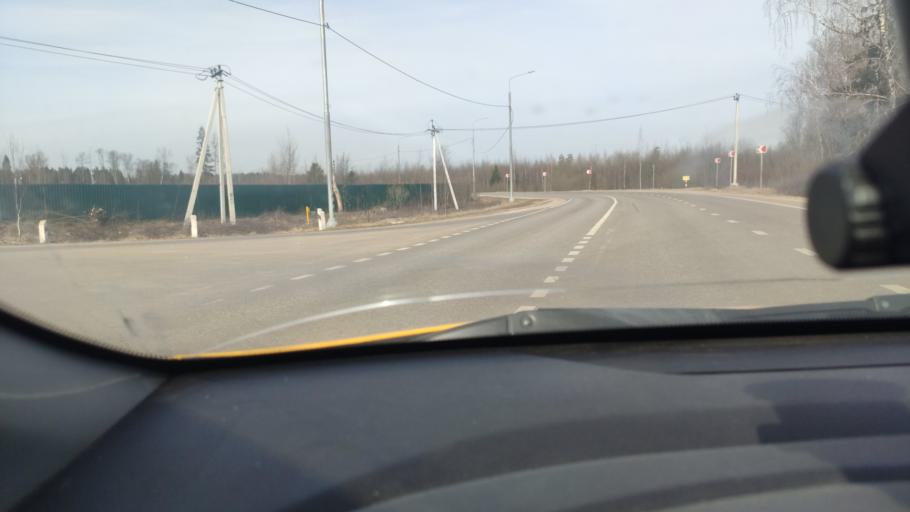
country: RU
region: Moskovskaya
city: Ruza
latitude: 55.7622
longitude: 36.1439
